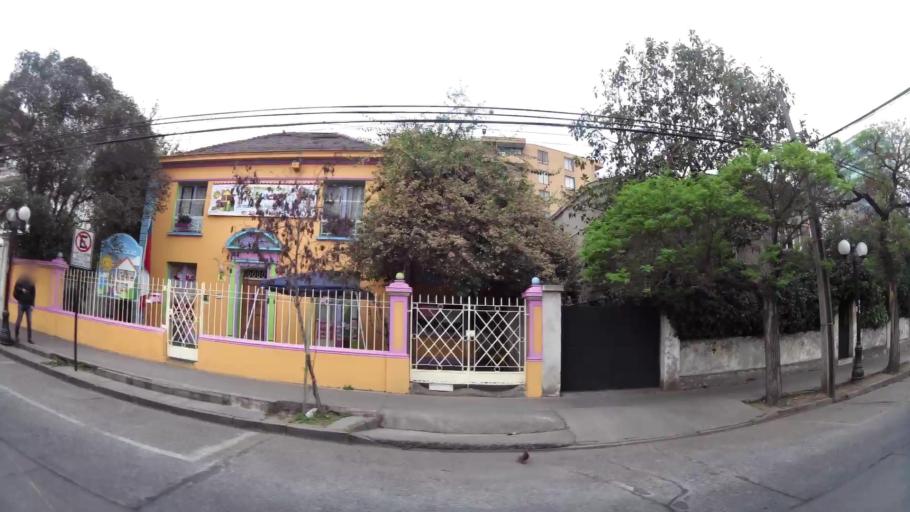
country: CL
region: Santiago Metropolitan
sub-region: Provincia de Santiago
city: Santiago
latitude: -33.4319
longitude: -70.6161
